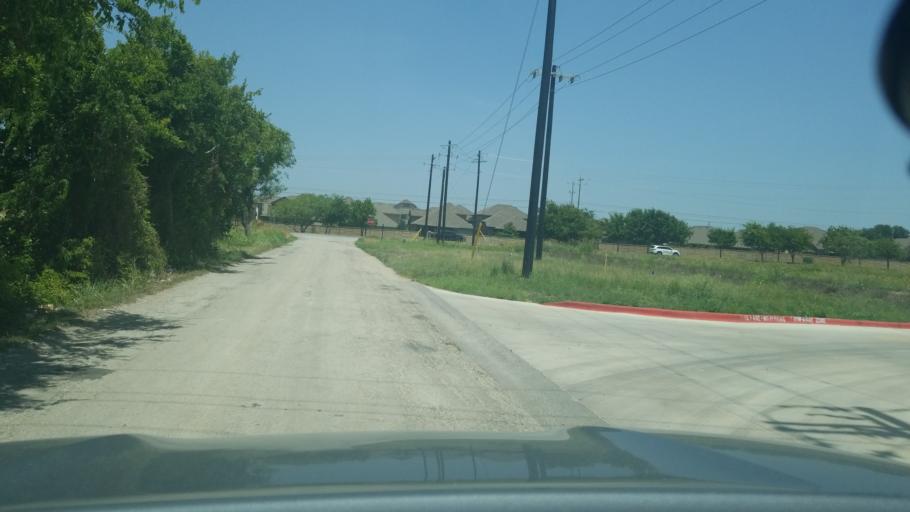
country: US
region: Texas
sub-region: Guadalupe County
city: Northcliff
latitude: 29.5971
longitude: -98.2210
